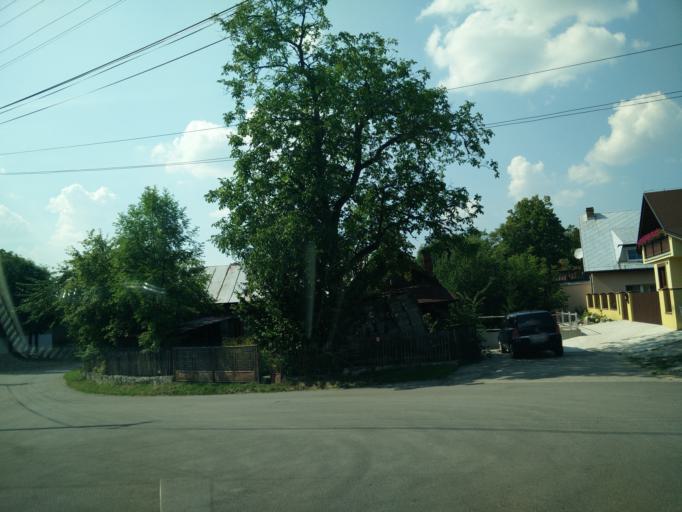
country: SK
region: Zilinsky
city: Rajec
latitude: 49.0586
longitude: 18.6574
